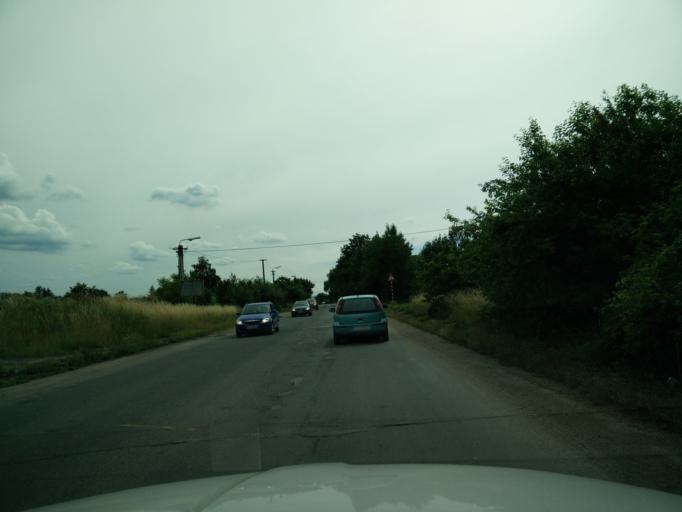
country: SK
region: Nitriansky
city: Bojnice
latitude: 48.7448
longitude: 18.5789
